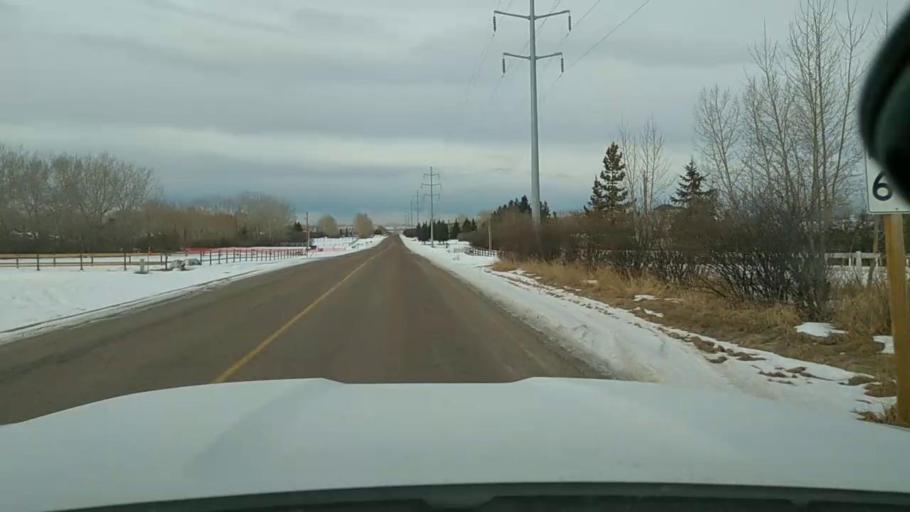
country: CA
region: Alberta
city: Airdrie
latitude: 51.2417
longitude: -113.9734
